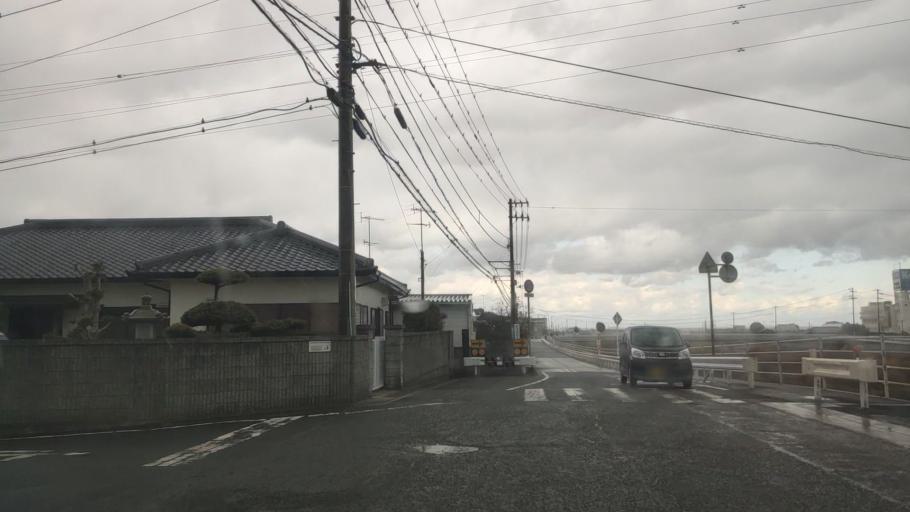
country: JP
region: Tokushima
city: Ishii
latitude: 34.2129
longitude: 134.4056
